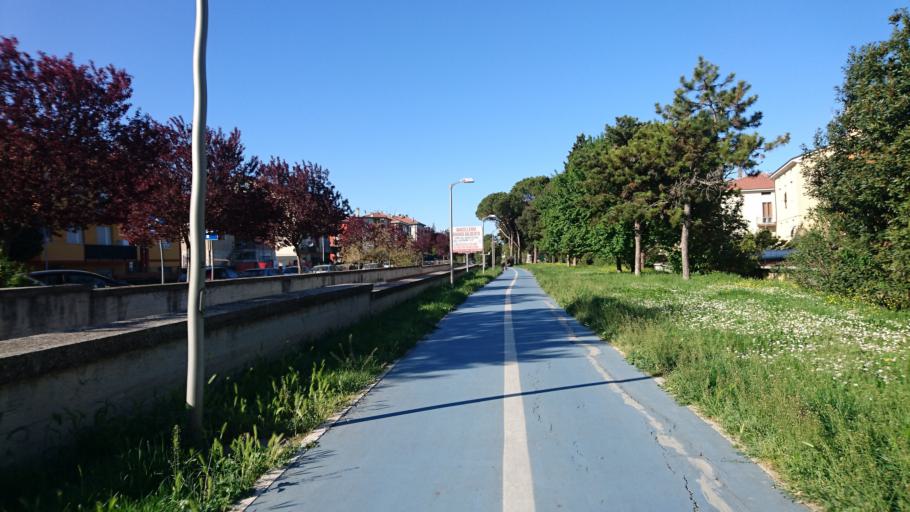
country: IT
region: The Marches
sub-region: Provincia di Pesaro e Urbino
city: Pesaro
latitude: 43.8987
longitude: 12.9122
